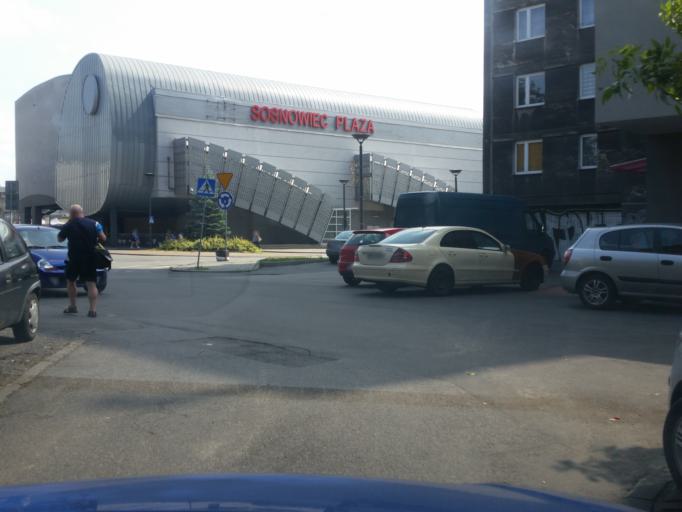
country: PL
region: Silesian Voivodeship
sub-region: Sosnowiec
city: Sosnowiec
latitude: 50.2759
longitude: 19.1261
